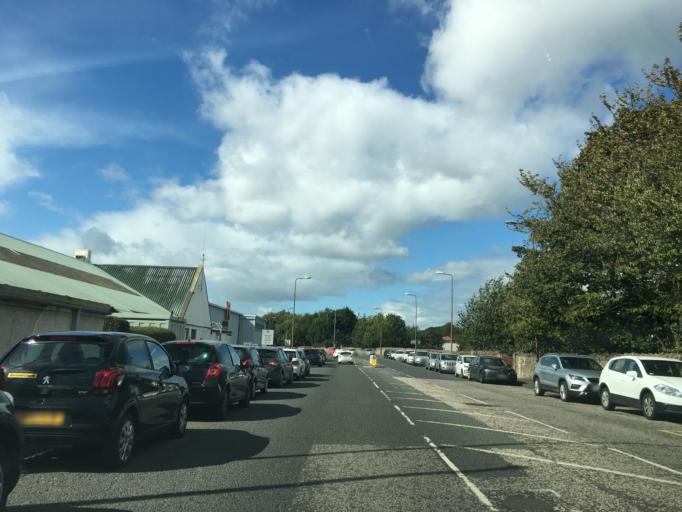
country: GB
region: Scotland
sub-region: West Lothian
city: Seafield
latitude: 55.9323
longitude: -3.1508
